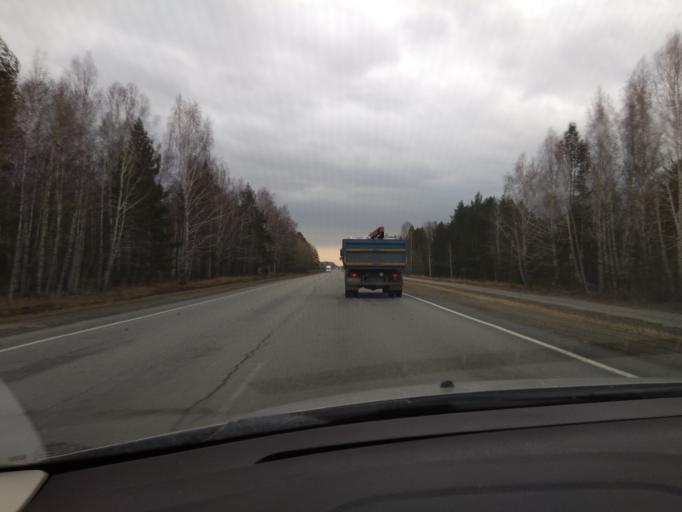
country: RU
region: Chelyabinsk
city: Tyubuk
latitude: 55.8936
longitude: 61.1314
